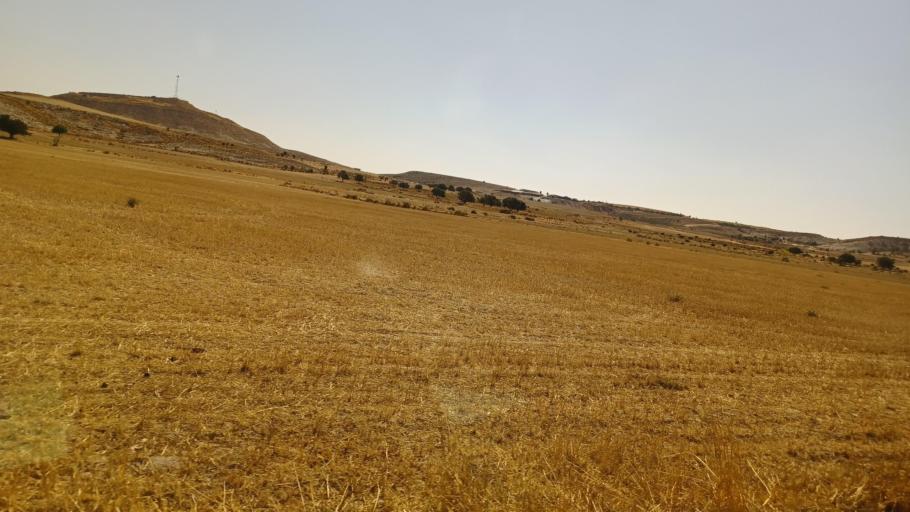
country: CY
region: Larnaka
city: Athienou
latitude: 35.0317
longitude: 33.5126
